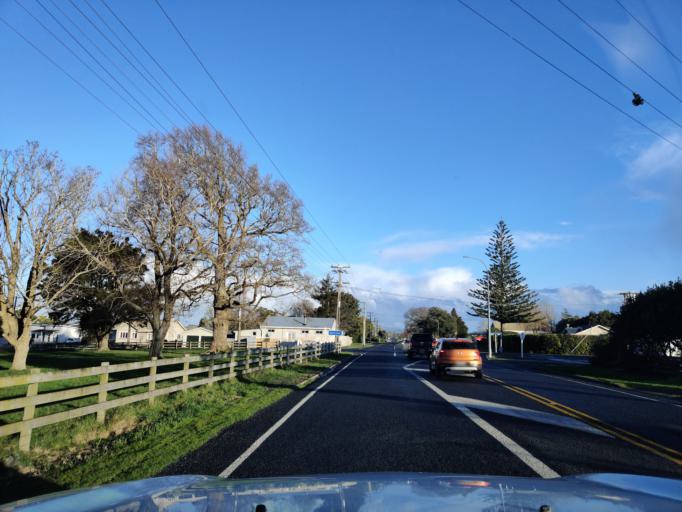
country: NZ
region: Waikato
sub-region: Hauraki District
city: Paeroa
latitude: -37.5887
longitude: 175.5022
